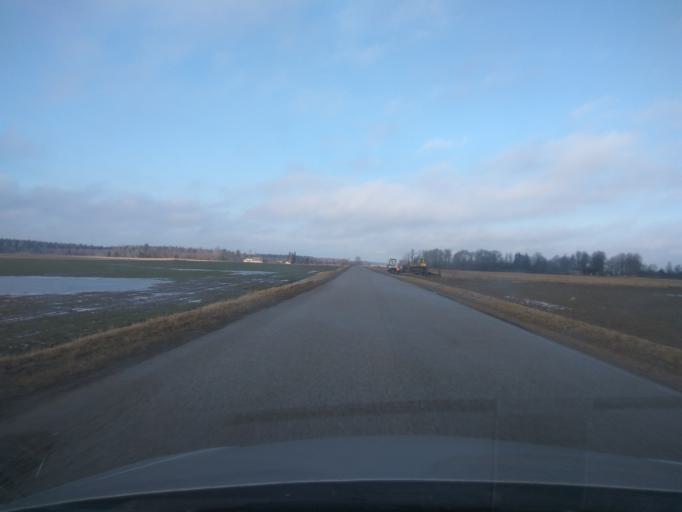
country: LV
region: Saldus Rajons
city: Saldus
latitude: 56.7947
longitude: 22.3844
